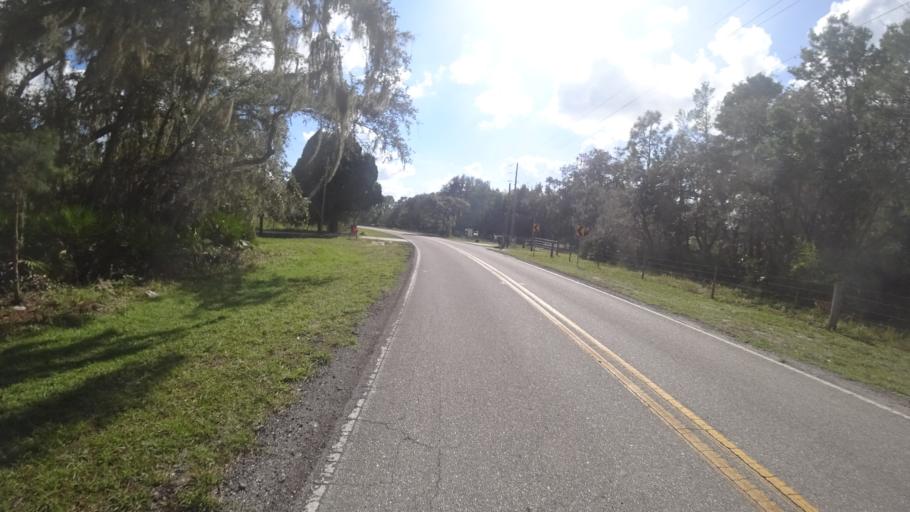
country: US
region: Florida
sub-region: Hillsborough County
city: Wimauma
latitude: 27.4308
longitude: -82.1329
